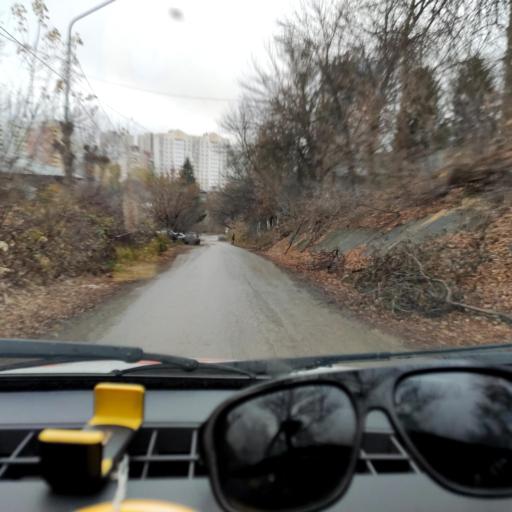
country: RU
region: Bashkortostan
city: Ufa
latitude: 54.7156
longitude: 55.9668
